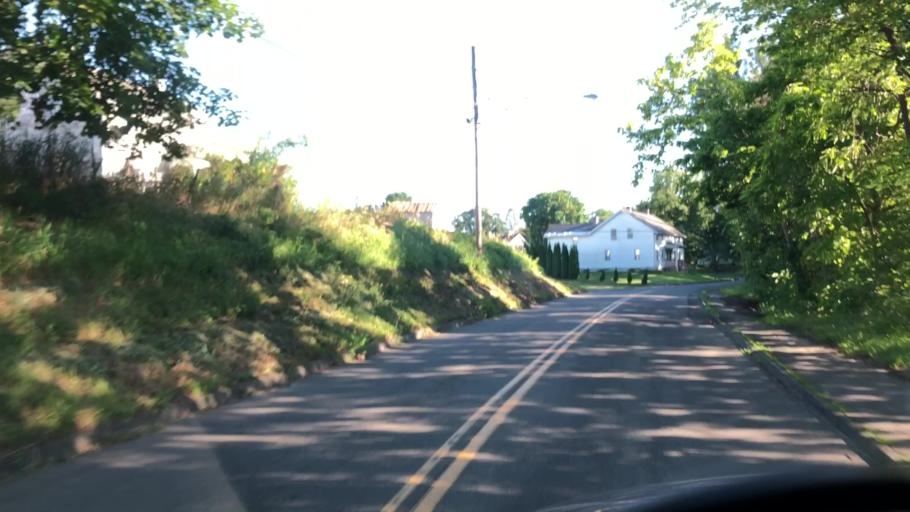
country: US
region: Massachusetts
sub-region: Hampshire County
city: Easthampton
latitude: 42.2754
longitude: -72.6546
